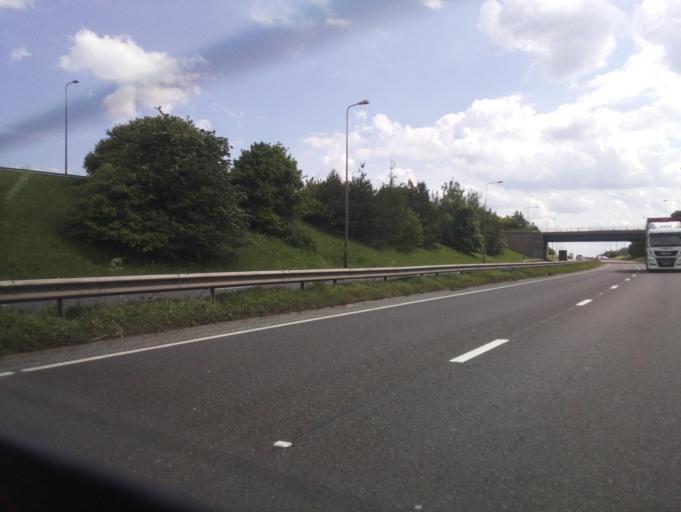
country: GB
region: England
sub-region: Hartlepool
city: Elwick
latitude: 54.7026
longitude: -1.3167
